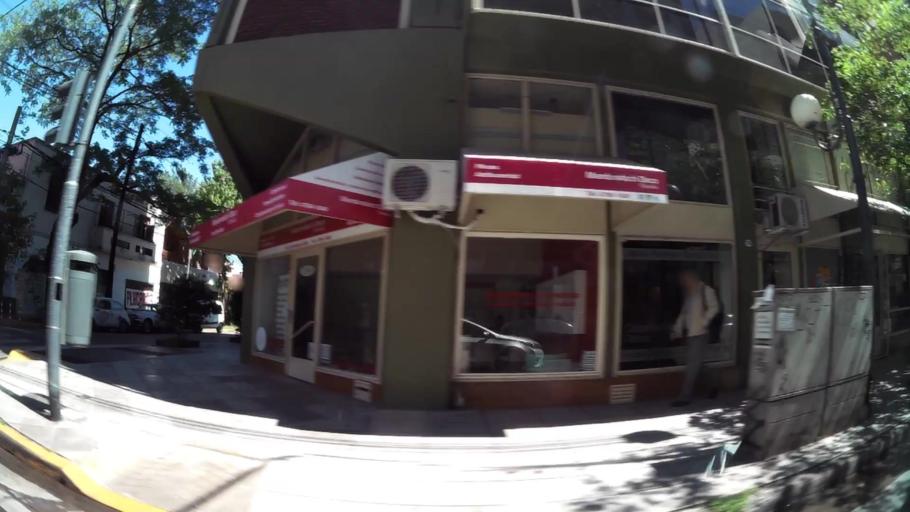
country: AR
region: Buenos Aires
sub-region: Partido de Vicente Lopez
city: Olivos
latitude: -34.5304
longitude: -58.4971
